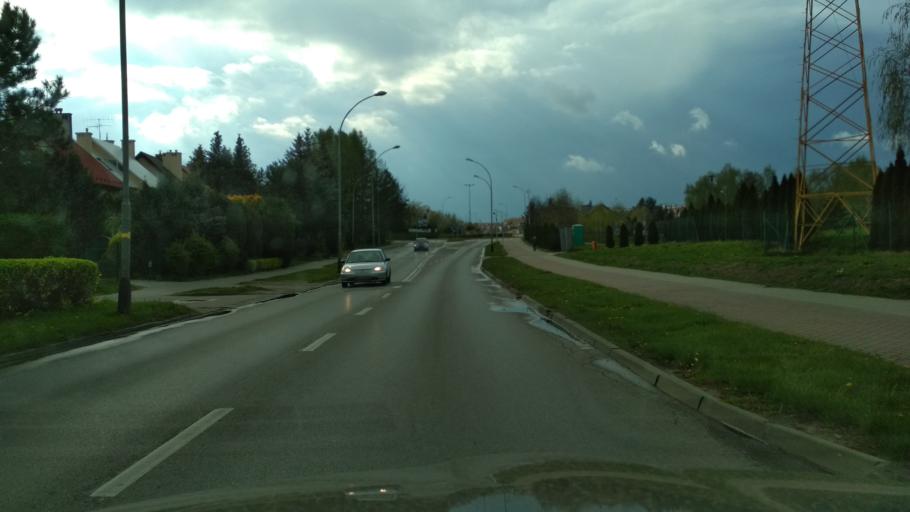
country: PL
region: Subcarpathian Voivodeship
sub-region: Rzeszow
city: Rzeszow
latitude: 50.0413
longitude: 21.9712
